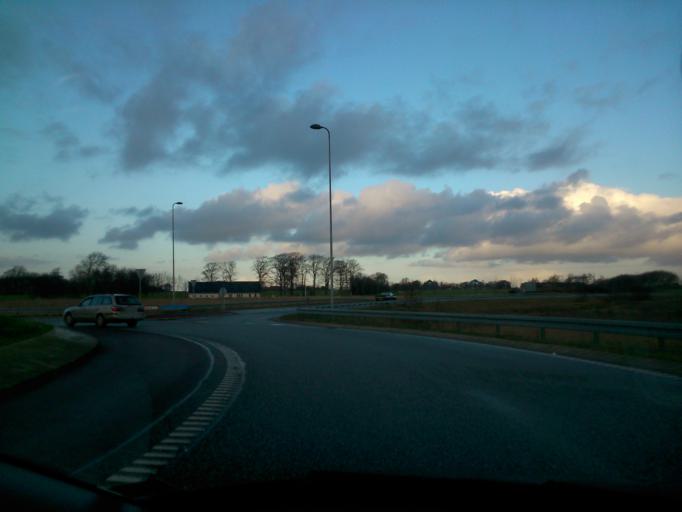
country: DK
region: Central Jutland
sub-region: Herning Kommune
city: Snejbjerg
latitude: 56.1277
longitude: 8.8739
